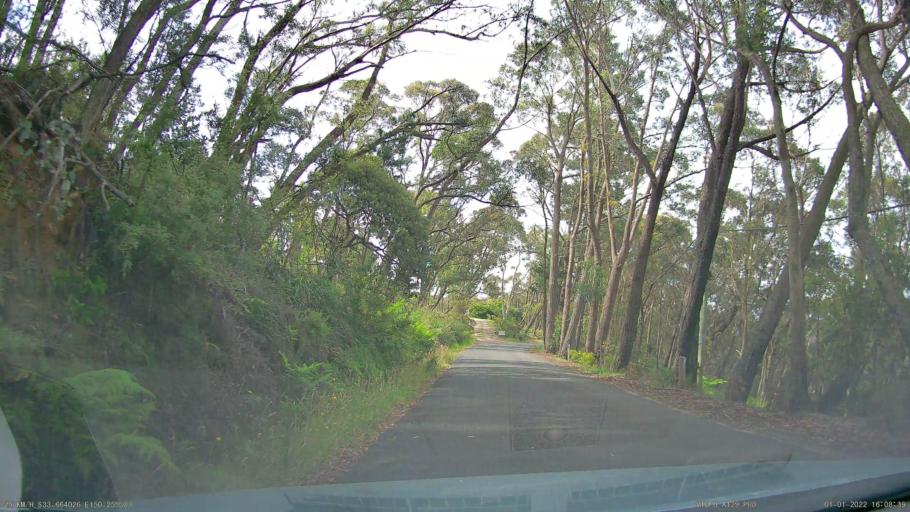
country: AU
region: New South Wales
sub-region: Blue Mountains Municipality
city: Blackheath
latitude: -33.6640
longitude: 150.2596
